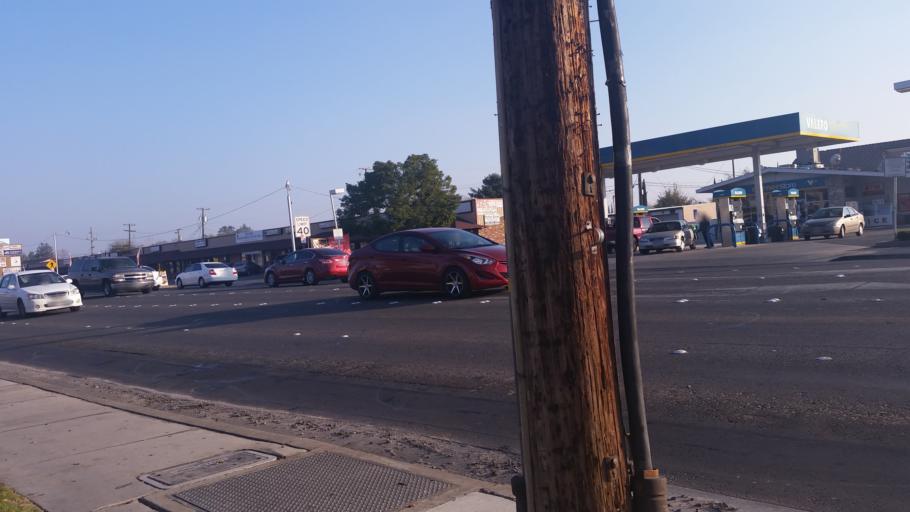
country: US
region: California
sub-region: Merced County
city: Atwater
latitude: 37.3606
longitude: -120.5957
